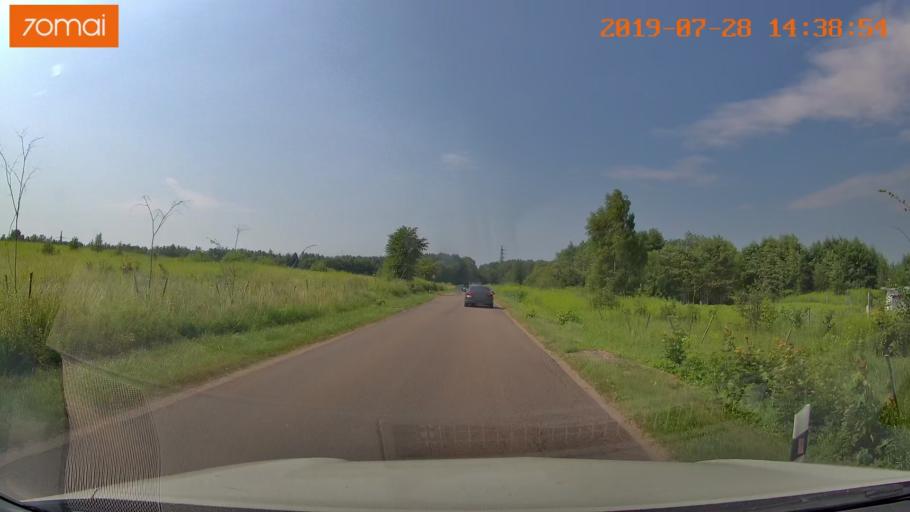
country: RU
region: Kaliningrad
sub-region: Gorod Kaliningrad
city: Yantarnyy
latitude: 54.8462
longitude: 19.9774
